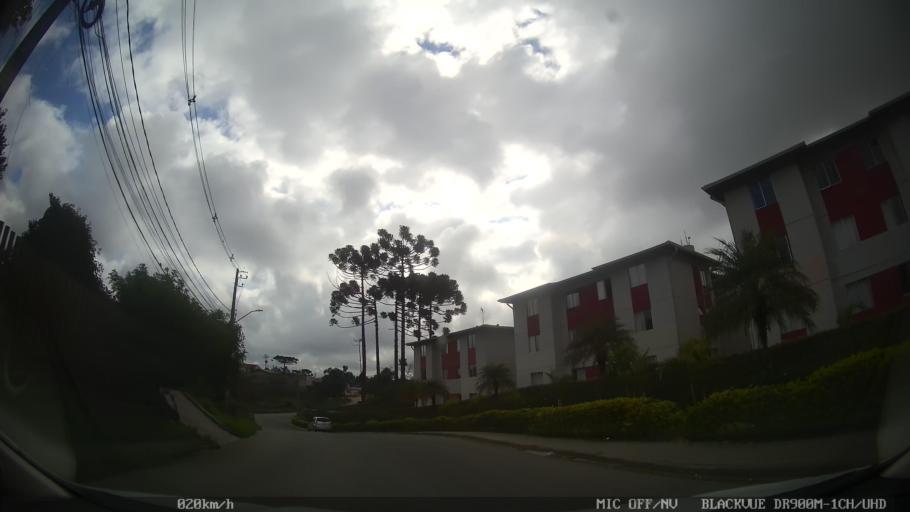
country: BR
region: Parana
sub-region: Colombo
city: Colombo
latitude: -25.3578
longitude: -49.2330
